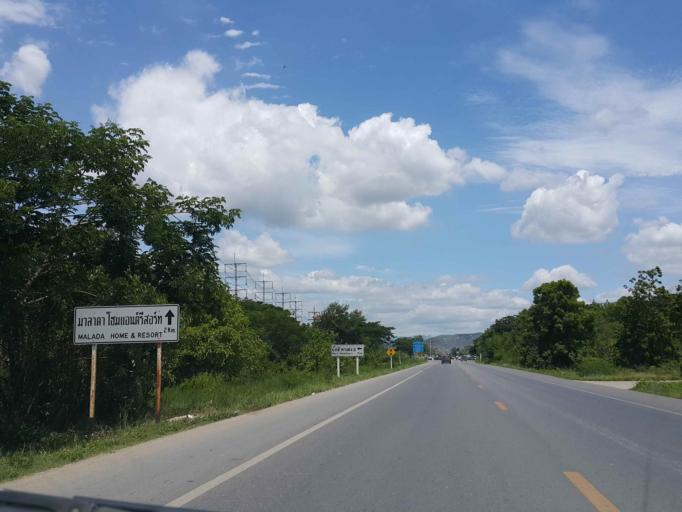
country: TH
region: Chiang Mai
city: Hang Dong
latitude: 18.7224
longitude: 98.9506
